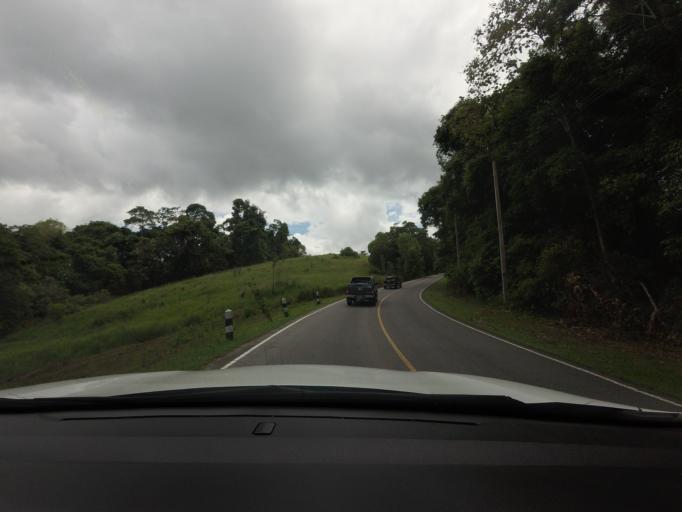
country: TH
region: Sara Buri
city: Muak Lek
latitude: 14.4475
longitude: 101.3673
